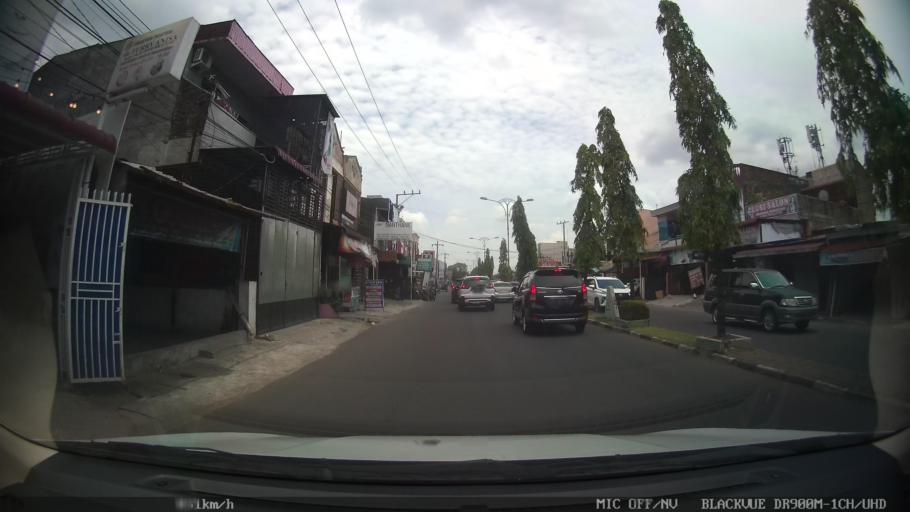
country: ID
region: North Sumatra
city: Medan
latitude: 3.5443
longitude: 98.6573
